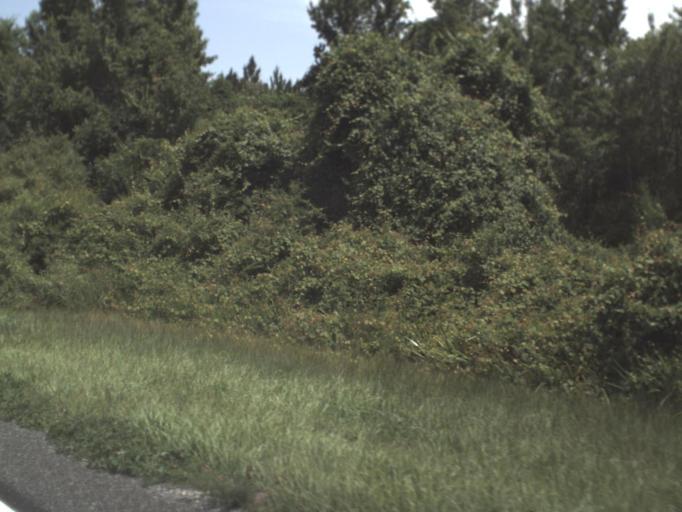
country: US
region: Florida
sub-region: Taylor County
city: Steinhatchee
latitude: 29.8655
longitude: -83.3935
